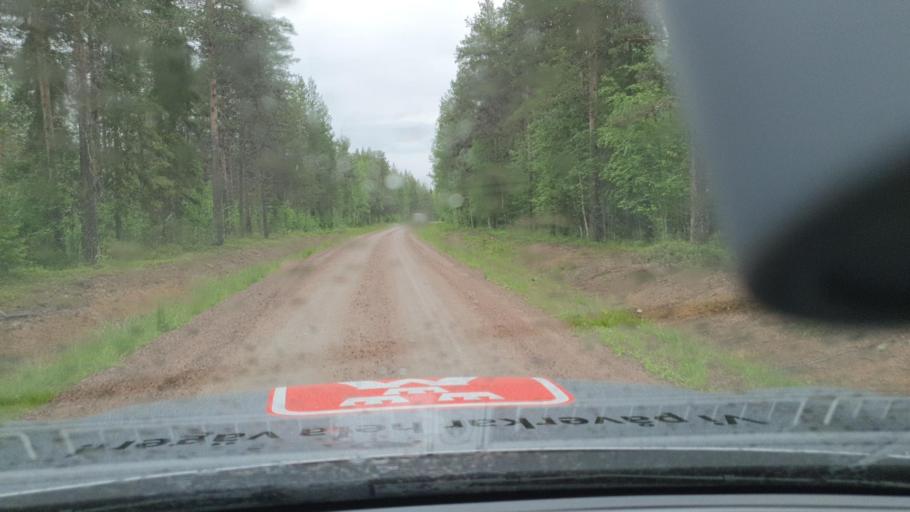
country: SE
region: Norrbotten
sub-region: Overkalix Kommun
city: OEverkalix
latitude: 66.5541
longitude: 22.7457
